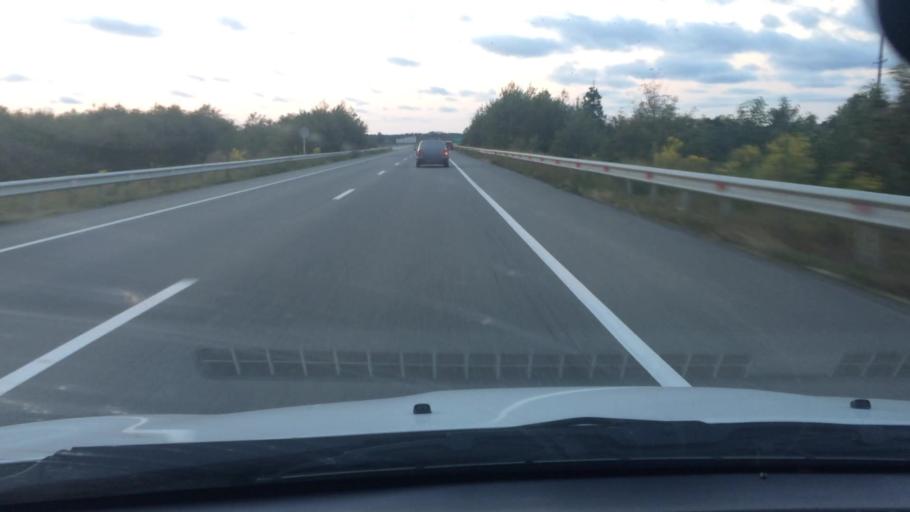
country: GE
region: Ajaria
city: Ochkhamuri
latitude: 41.9077
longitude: 41.7860
